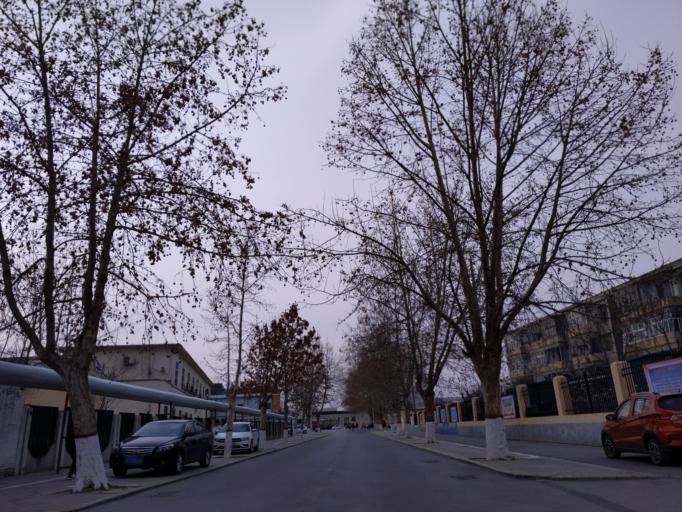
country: CN
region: Henan Sheng
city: Zhongyuanlu
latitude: 35.7601
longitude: 115.0432
